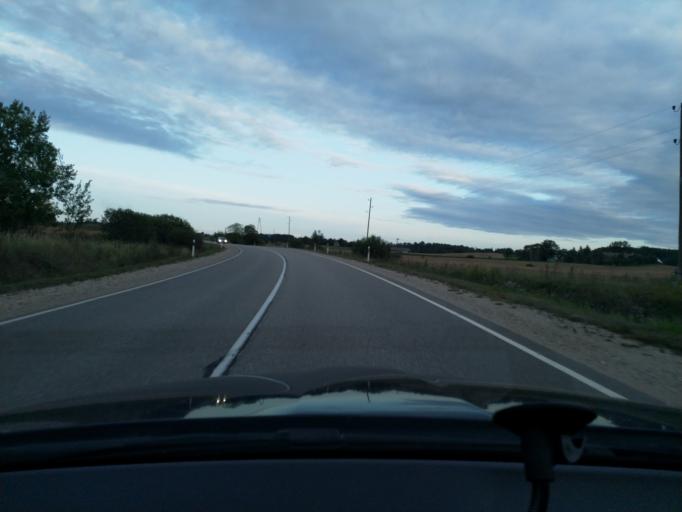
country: LV
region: Kandava
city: Kandava
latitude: 56.9312
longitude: 22.7454
